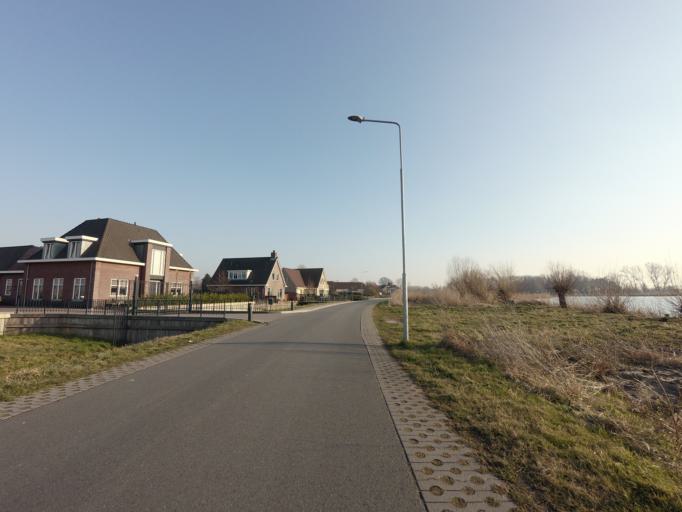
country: NL
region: North Holland
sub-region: Gemeente Haarlem
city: Haarlem
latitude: 52.3904
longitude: 4.6825
